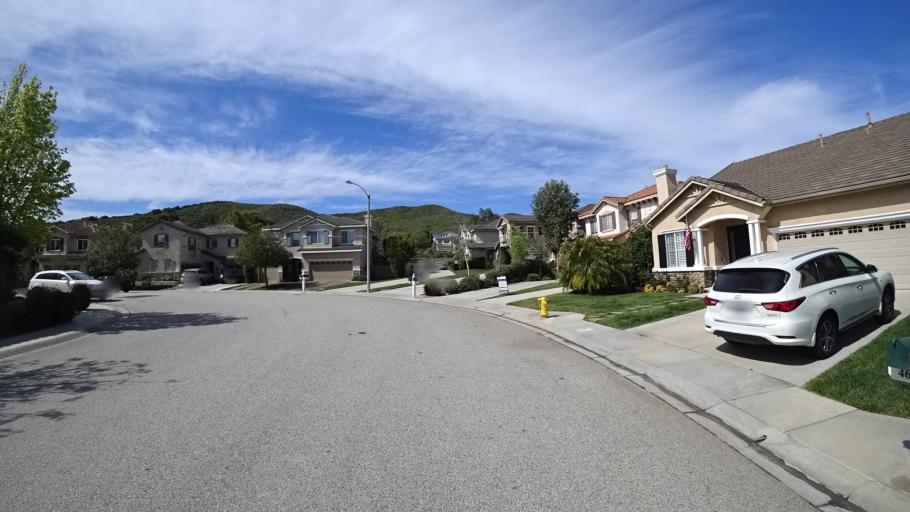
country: US
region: California
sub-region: Ventura County
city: Casa Conejo
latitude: 34.1716
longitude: -118.9747
